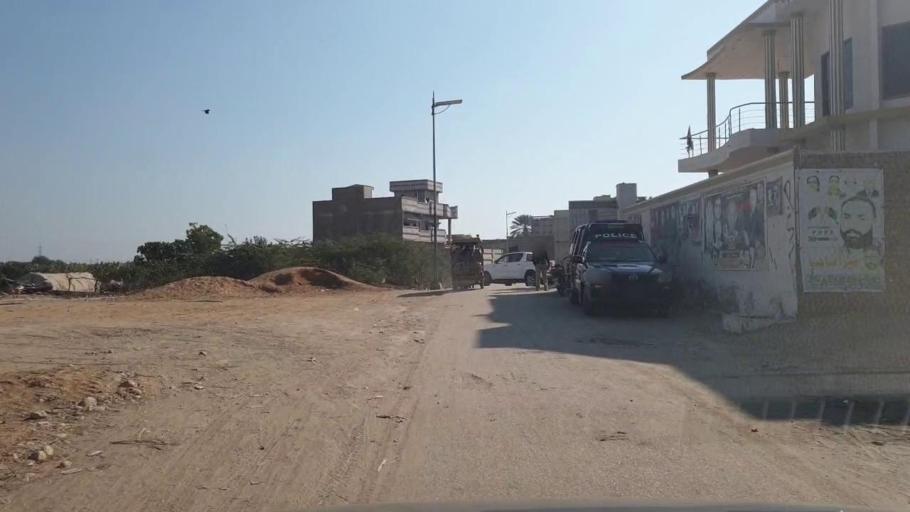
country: PK
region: Sindh
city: Shahpur Chakar
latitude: 26.1511
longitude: 68.6499
